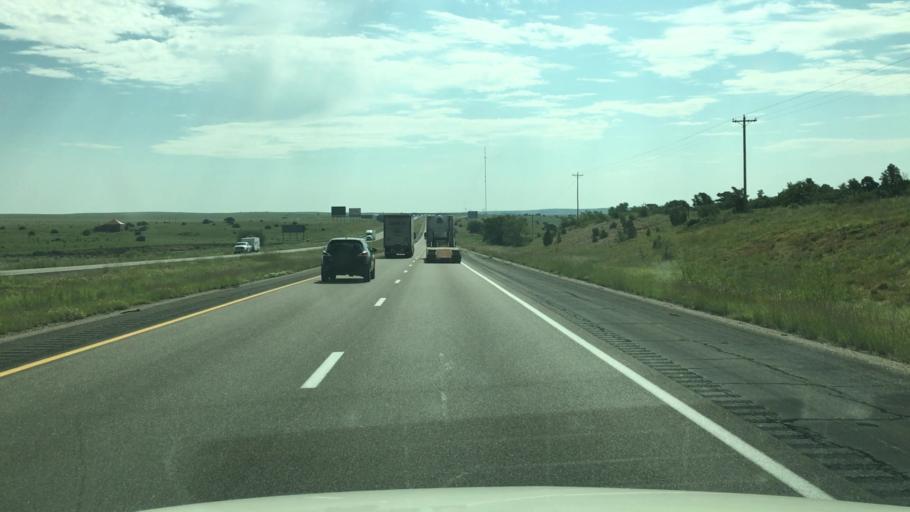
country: US
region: New Mexico
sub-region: San Miguel County
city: Las Vegas
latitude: 34.9922
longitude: -105.3106
